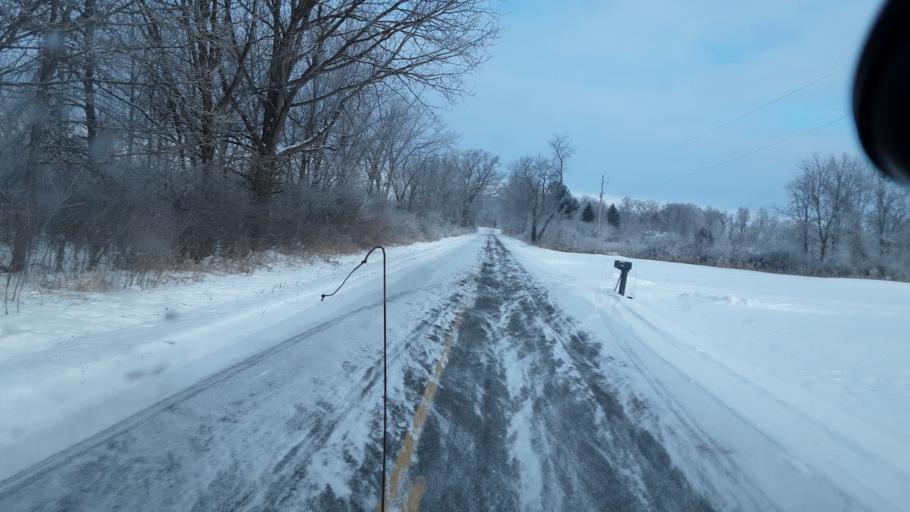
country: US
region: Michigan
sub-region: Ingham County
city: Leslie
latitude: 42.4178
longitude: -84.4823
